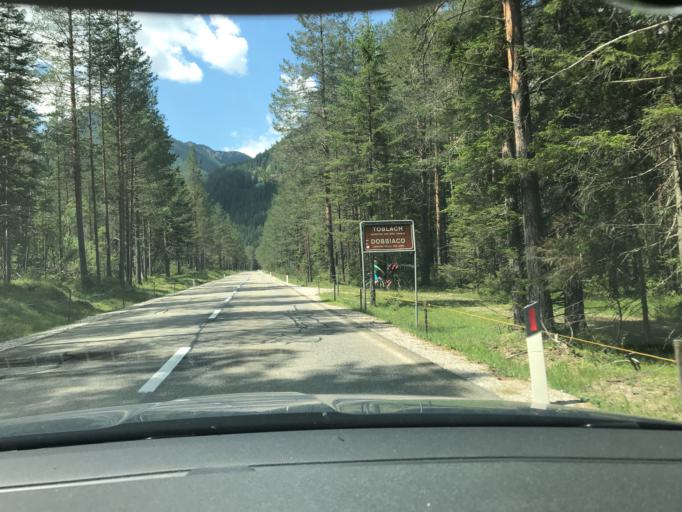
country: IT
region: Trentino-Alto Adige
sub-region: Bolzano
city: Dobbiaco
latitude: 46.6145
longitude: 12.2242
